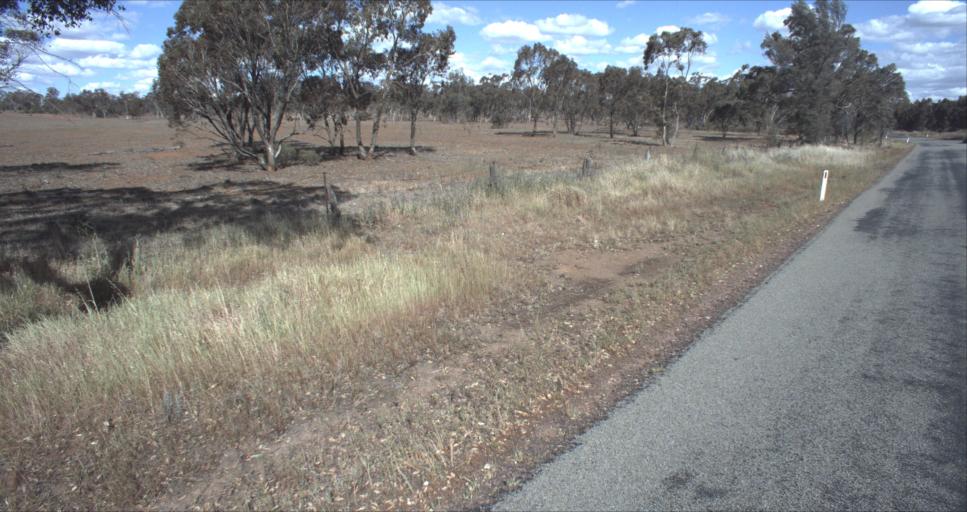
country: AU
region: New South Wales
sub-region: Griffith
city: Griffith
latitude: -34.4079
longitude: 146.2159
